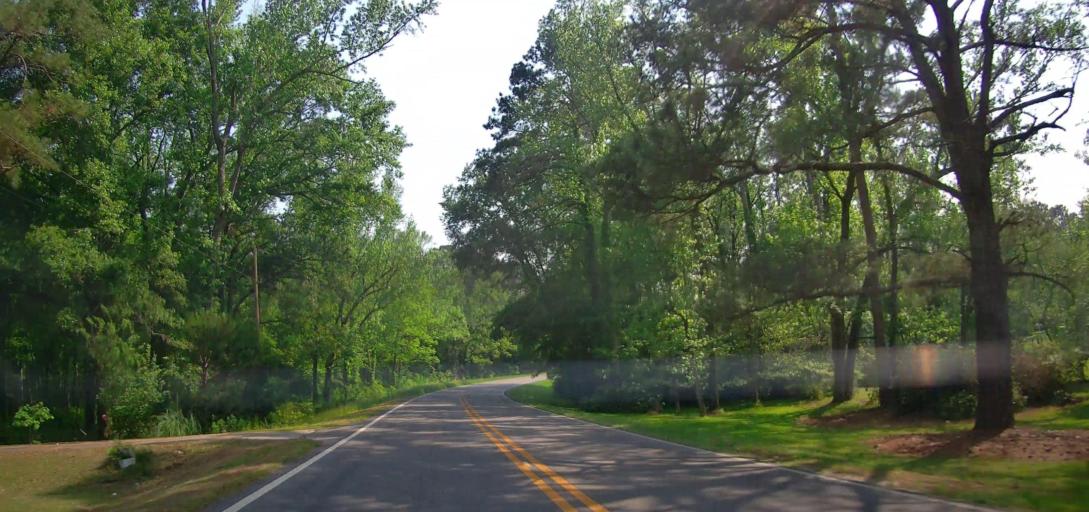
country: US
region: Georgia
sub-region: Laurens County
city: East Dublin
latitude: 32.5659
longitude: -82.8654
